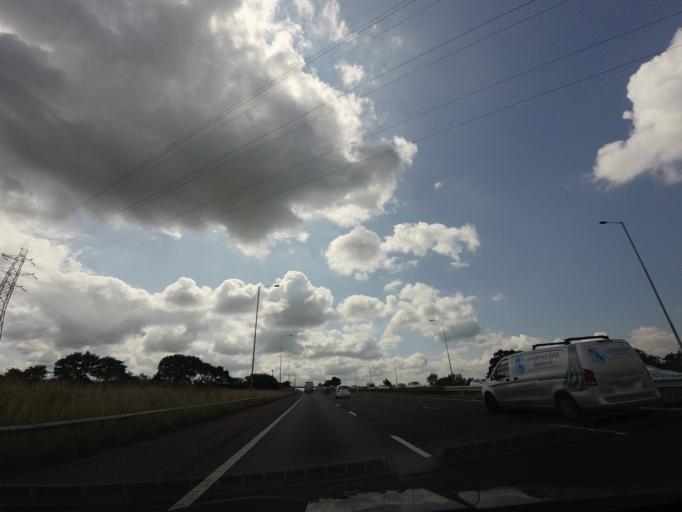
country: GB
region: England
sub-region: Lancashire
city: Euxton
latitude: 53.6474
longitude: -2.6918
